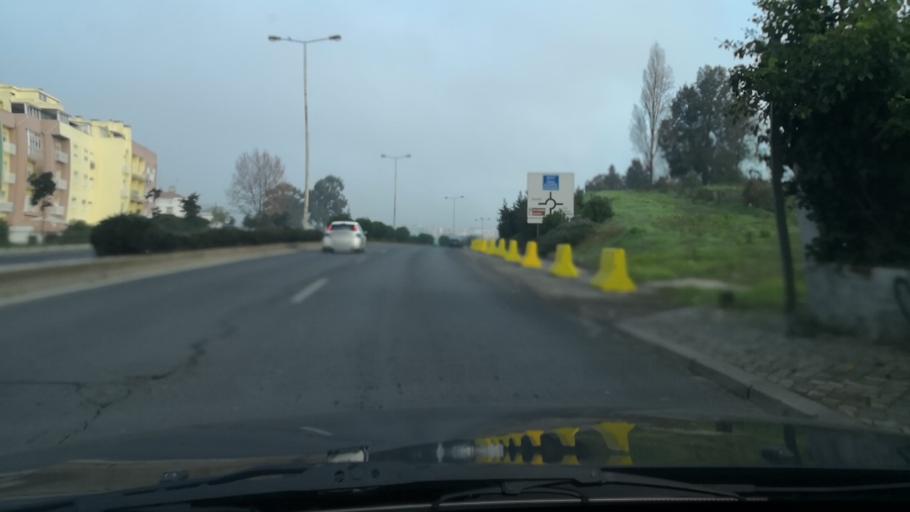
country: PT
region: Setubal
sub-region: Setubal
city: Setubal
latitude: 38.5334
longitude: -8.8754
